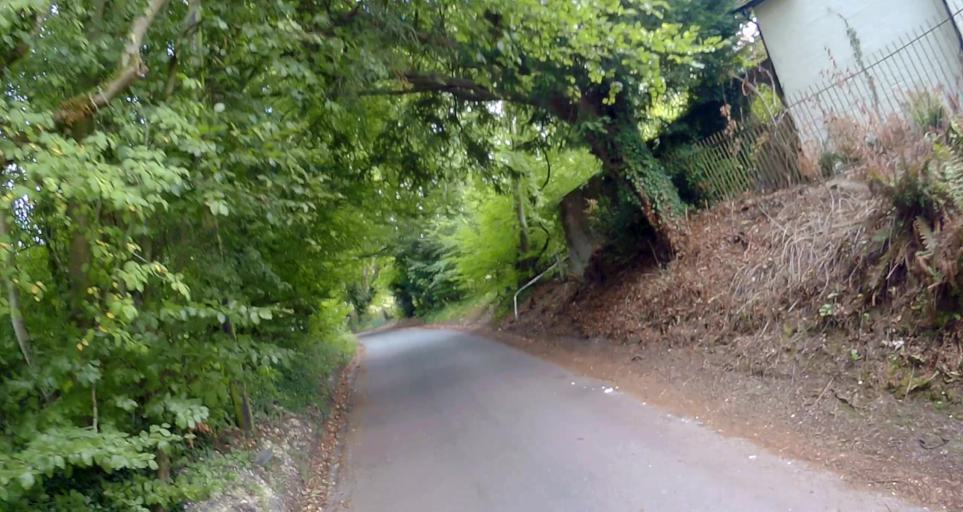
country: GB
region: England
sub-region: Hampshire
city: Kings Worthy
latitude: 51.0809
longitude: -1.1932
